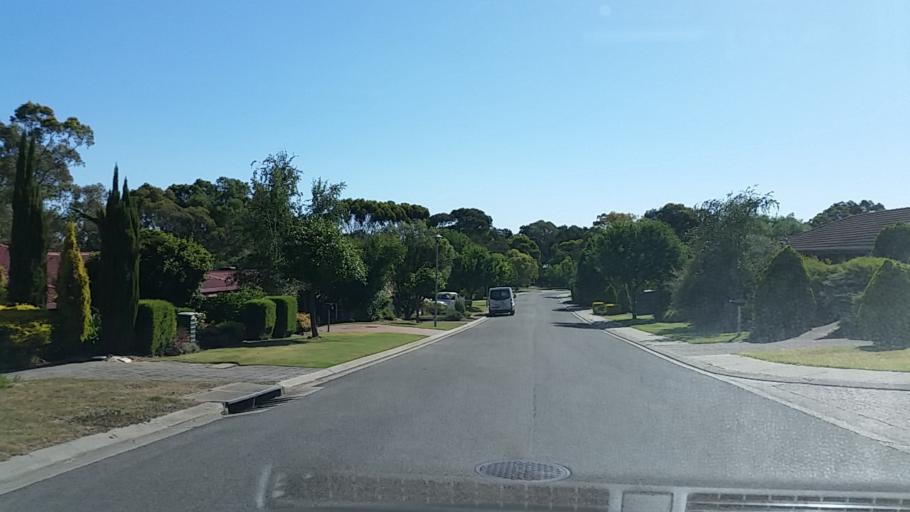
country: AU
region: South Australia
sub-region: Tea Tree Gully
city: Golden Grove
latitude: -34.7968
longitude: 138.7027
